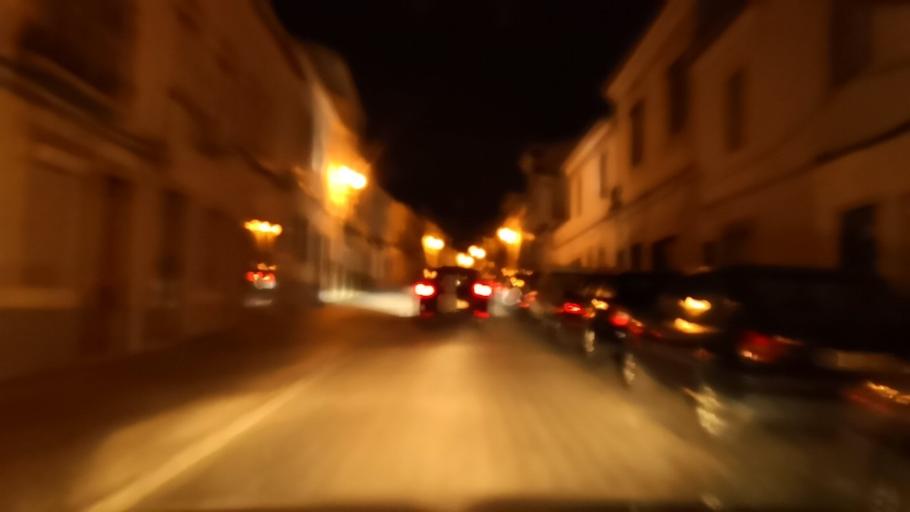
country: PT
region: Evora
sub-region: Estremoz
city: Estremoz
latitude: 38.8452
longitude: -7.5903
